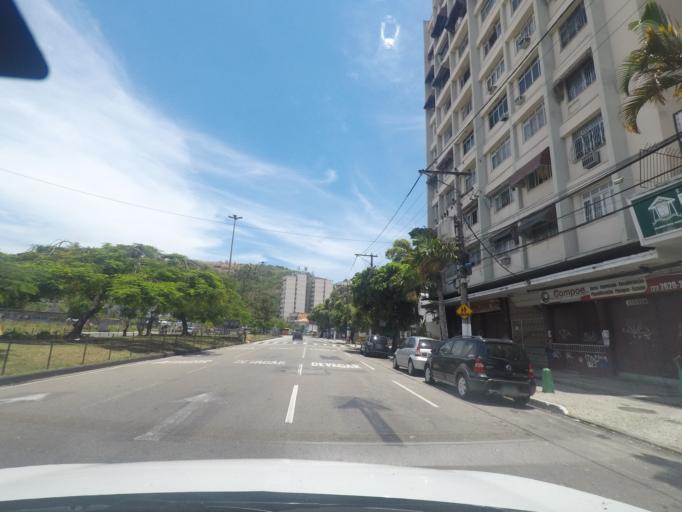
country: BR
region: Rio de Janeiro
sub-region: Niteroi
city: Niteroi
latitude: -22.8873
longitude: -43.1246
